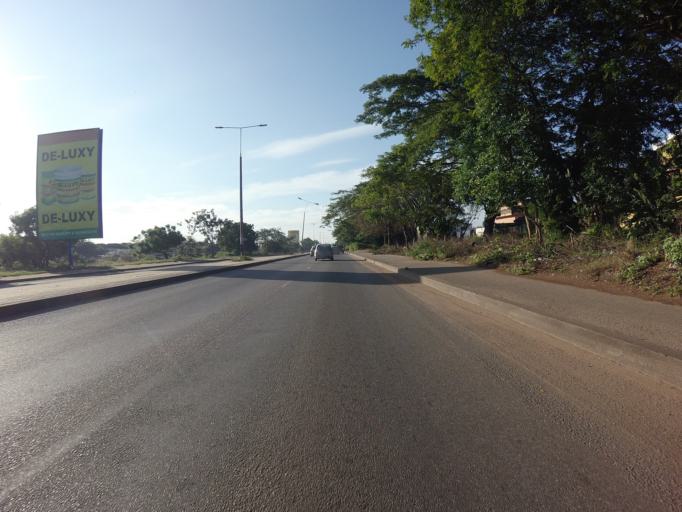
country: GH
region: Greater Accra
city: Accra
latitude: 5.5475
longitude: -0.2285
